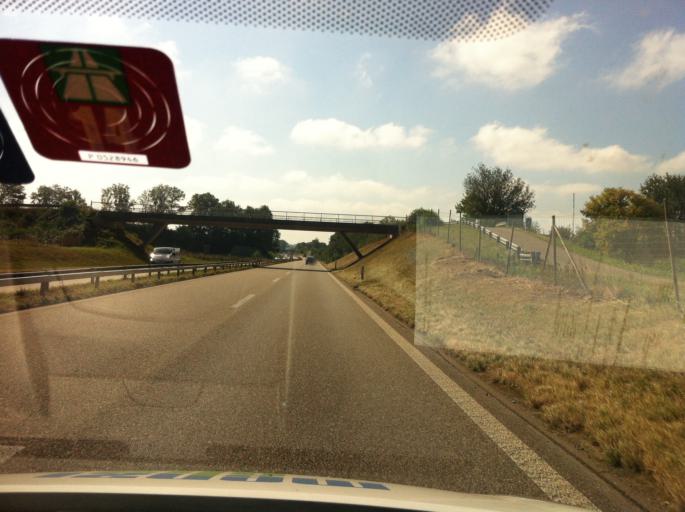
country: CH
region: Zurich
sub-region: Bezirk Buelach
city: Bachenbulach
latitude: 47.4808
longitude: 8.5495
